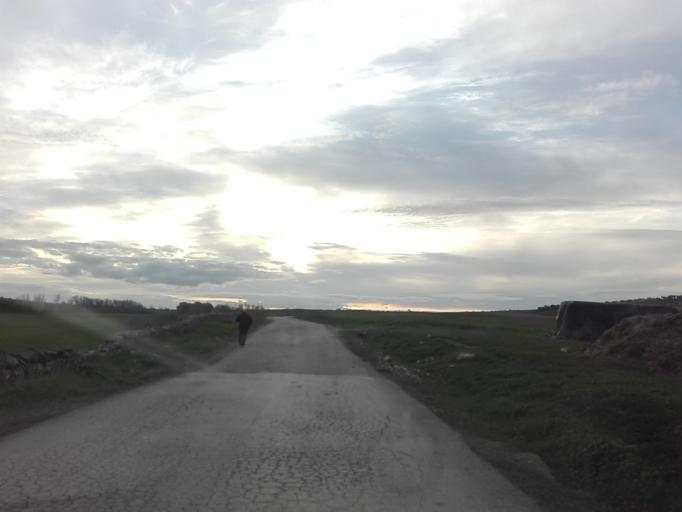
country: ES
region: Extremadura
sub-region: Provincia de Badajoz
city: Usagre
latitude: 38.3600
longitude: -6.1688
